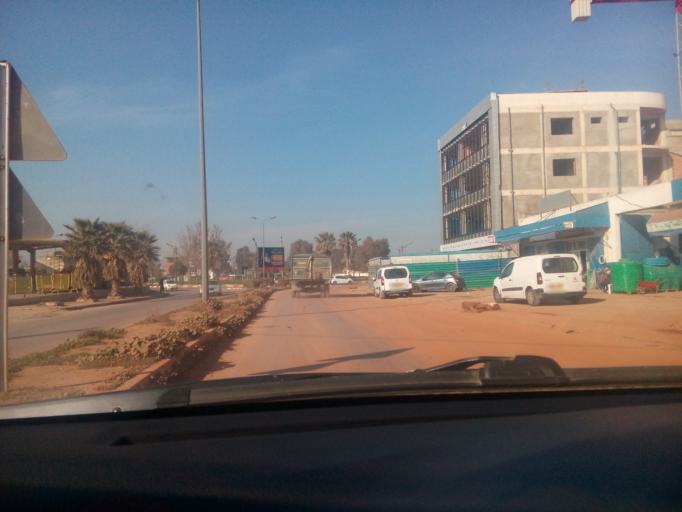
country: DZ
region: Oran
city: Es Senia
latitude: 35.6483
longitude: -0.6111
